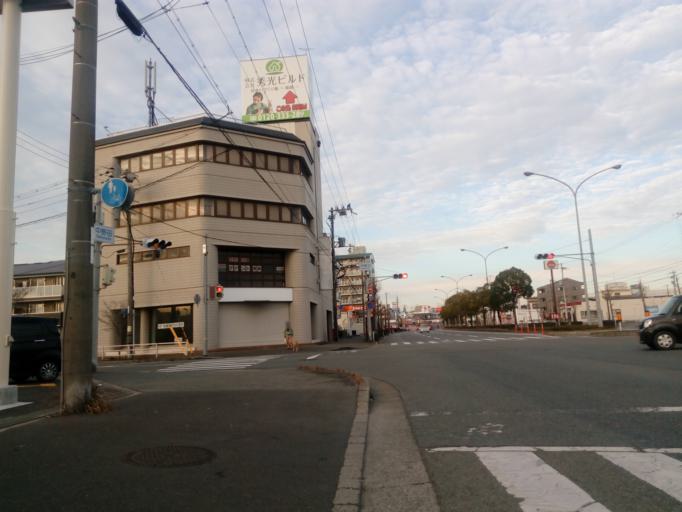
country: JP
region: Hyogo
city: Himeji
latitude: 34.8056
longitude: 134.6801
